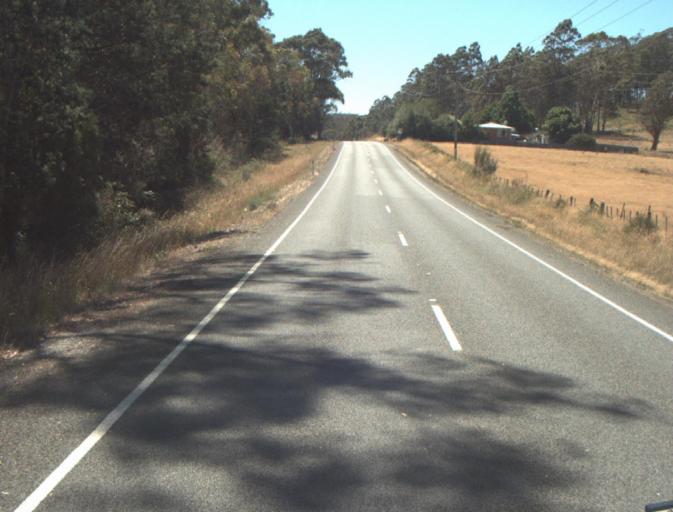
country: AU
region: Tasmania
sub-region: Launceston
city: Newstead
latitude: -41.3883
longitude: 147.3032
